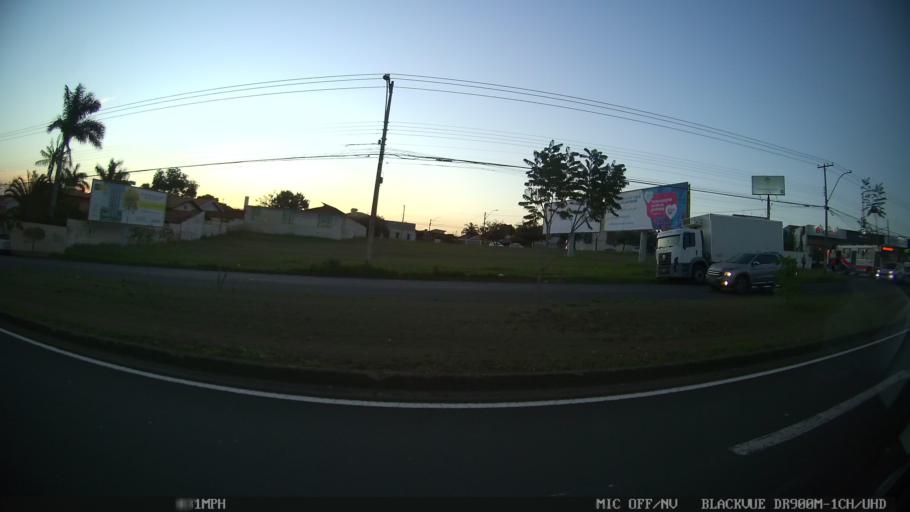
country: BR
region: Sao Paulo
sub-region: Sao Jose Do Rio Preto
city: Sao Jose do Rio Preto
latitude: -20.8082
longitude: -49.3492
